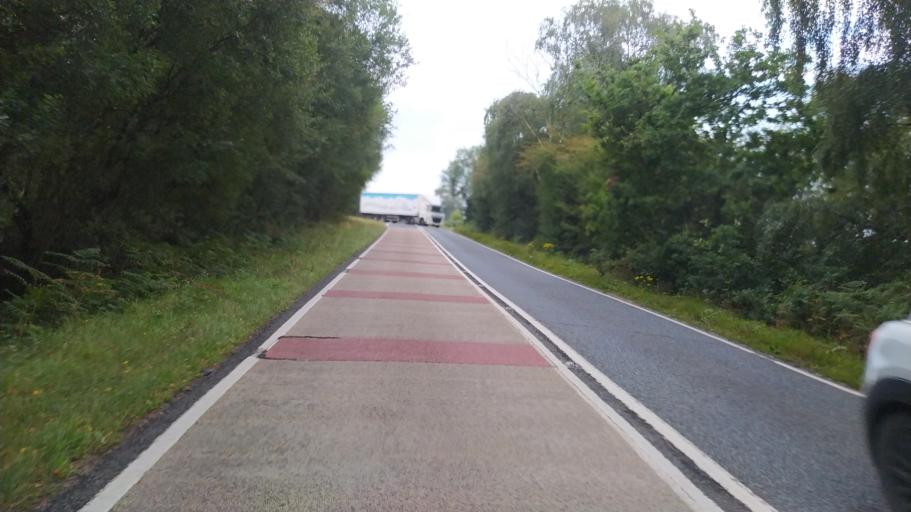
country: GB
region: England
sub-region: Hampshire
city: New Milton
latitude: 50.7957
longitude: -1.6800
